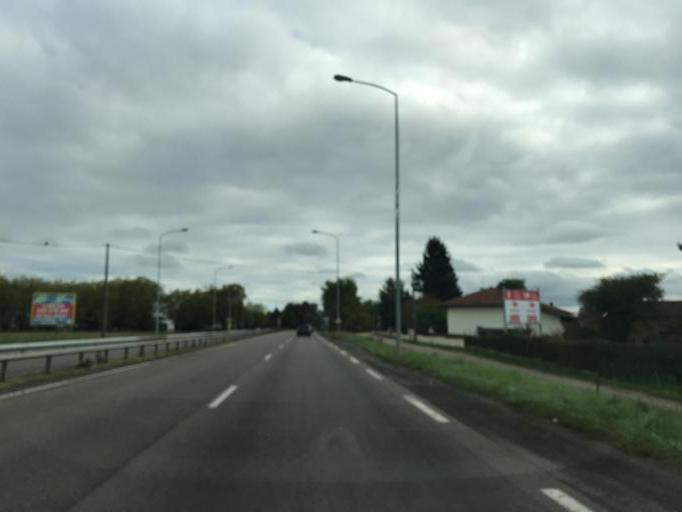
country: FR
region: Rhone-Alpes
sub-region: Departement de l'Ain
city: Saint-Denis-les-Bourg
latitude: 46.2271
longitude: 5.2046
